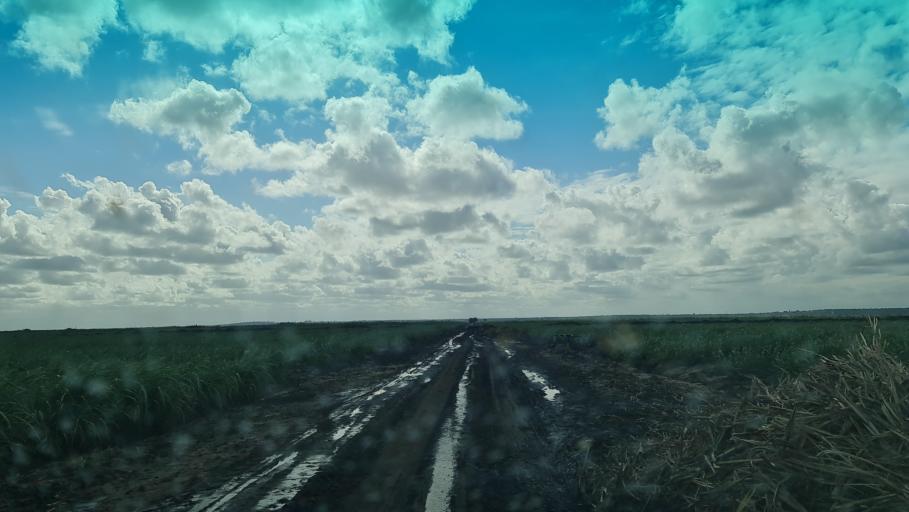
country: MZ
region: Maputo
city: Manhica
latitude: -25.4389
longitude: 32.8558
